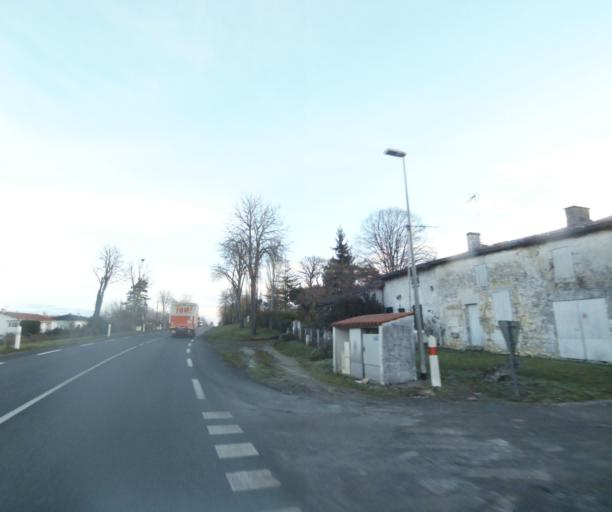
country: FR
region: Poitou-Charentes
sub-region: Departement de la Charente-Maritime
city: Fontcouverte
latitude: 45.7984
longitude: -0.5654
